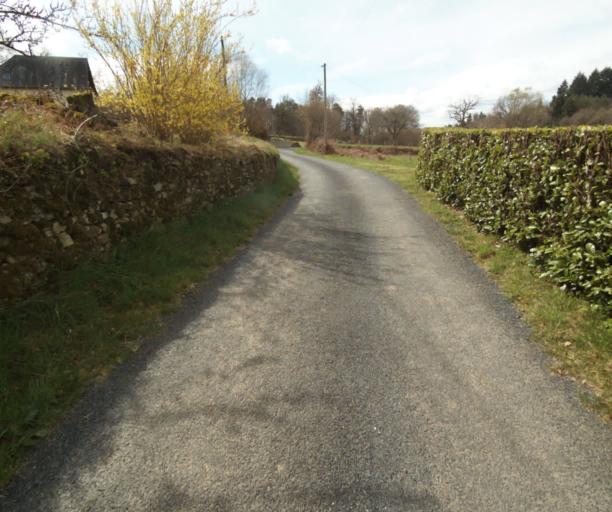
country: FR
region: Limousin
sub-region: Departement de la Correze
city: Correze
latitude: 45.3787
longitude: 1.9010
